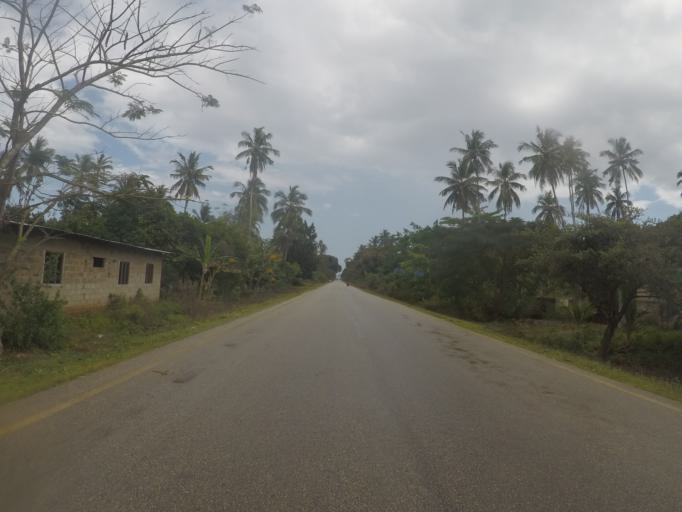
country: TZ
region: Zanzibar North
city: Mkokotoni
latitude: -5.9968
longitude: 39.1956
